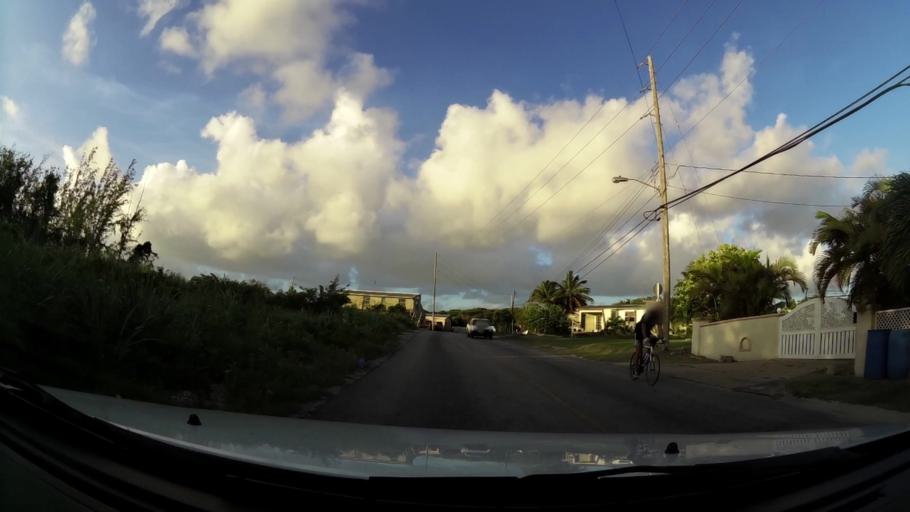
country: BB
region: Saint Philip
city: Crane
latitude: 13.0895
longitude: -59.4731
